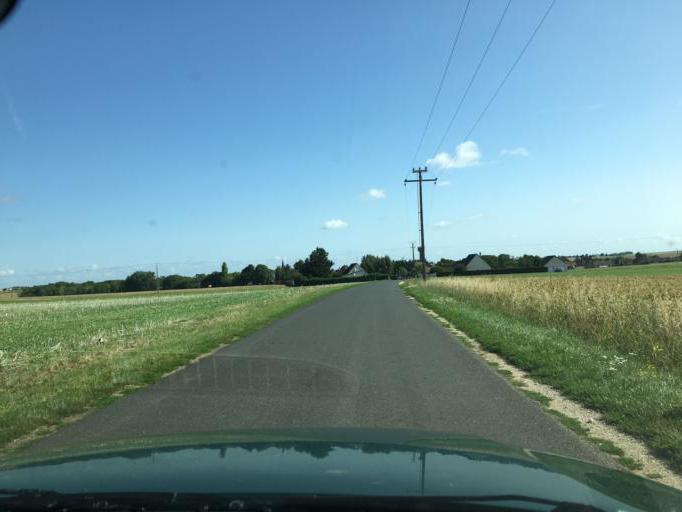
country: FR
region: Centre
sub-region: Departement du Loiret
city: Bricy
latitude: 48.0064
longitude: 1.7350
